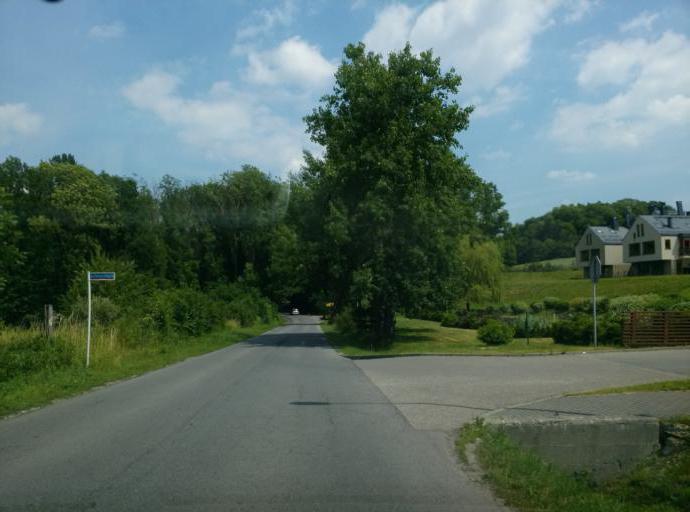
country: PL
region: Lesser Poland Voivodeship
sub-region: Powiat krakowski
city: Mogilany
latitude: 49.9444
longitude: 19.8773
